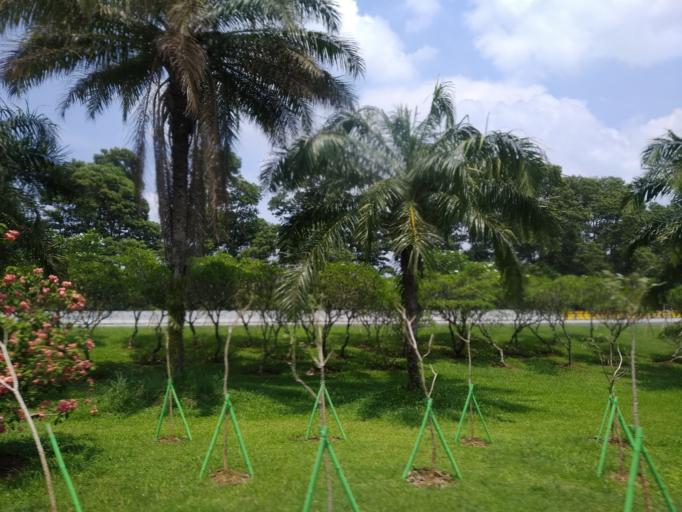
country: ID
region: West Java
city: Bogor
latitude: -6.5962
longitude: 106.8296
